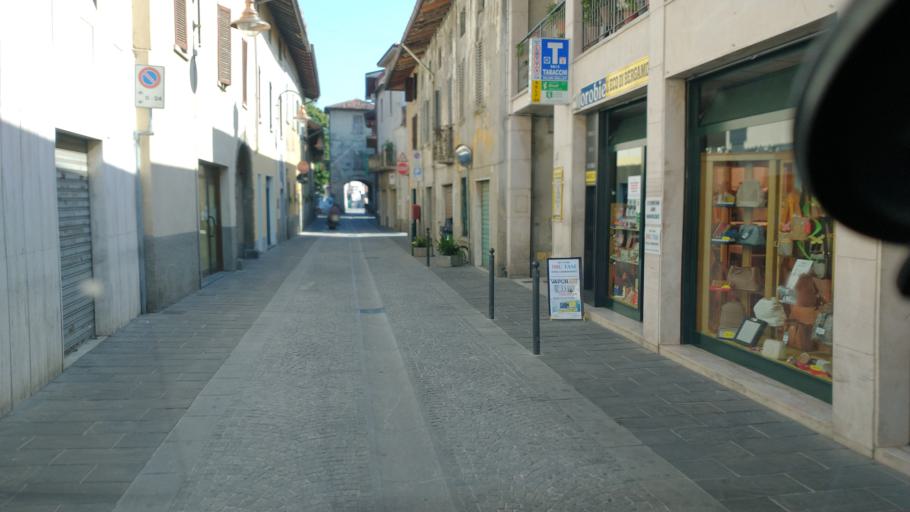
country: IT
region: Lombardy
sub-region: Provincia di Bergamo
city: Cologno al Serio
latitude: 45.5786
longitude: 9.7092
